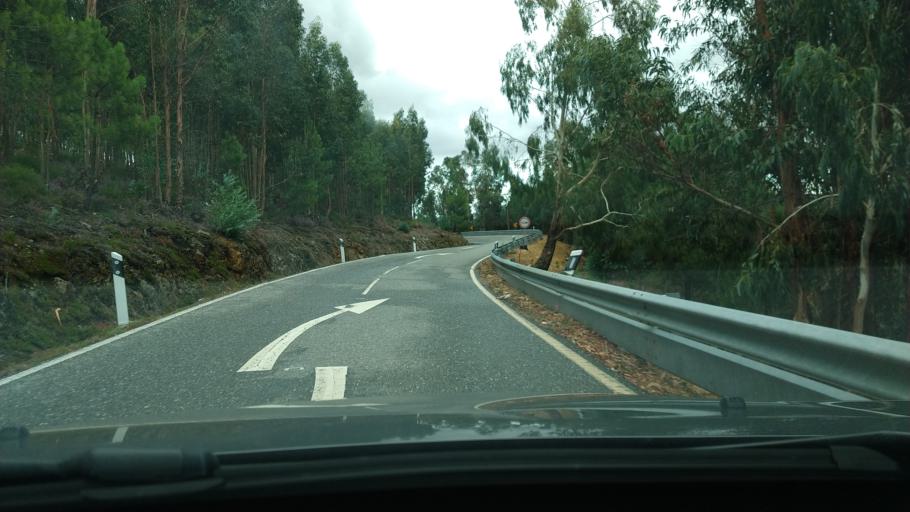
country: PT
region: Castelo Branco
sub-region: Covilha
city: Covilha
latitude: 40.2391
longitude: -7.6559
